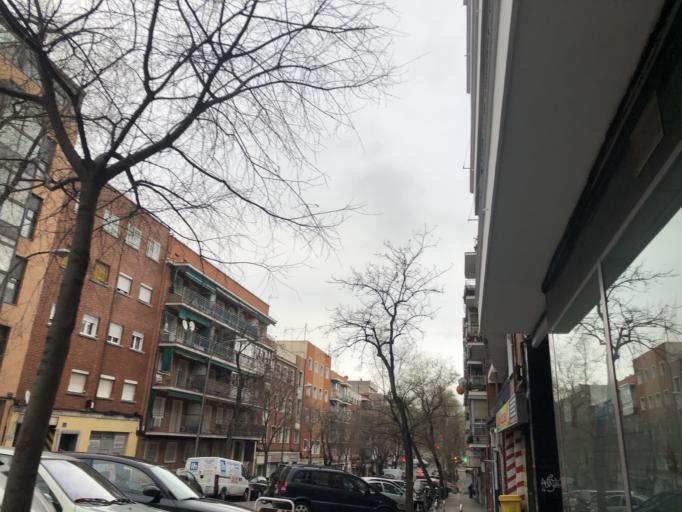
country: ES
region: Madrid
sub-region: Provincia de Madrid
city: Moratalaz
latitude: 40.4331
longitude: -3.6436
